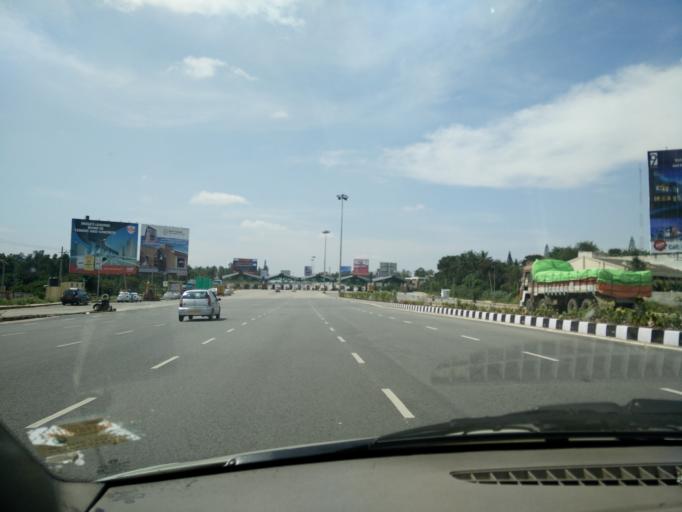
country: IN
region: Karnataka
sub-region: Bangalore Rural
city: Devanhalli
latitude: 13.1954
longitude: 77.6527
